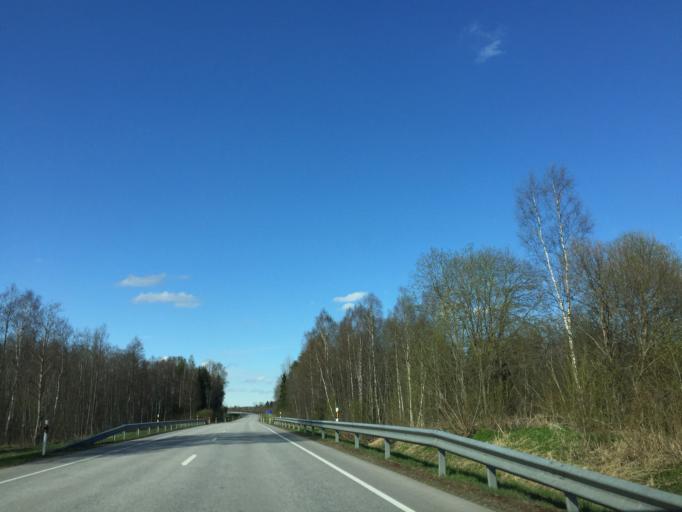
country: EE
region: Vorumaa
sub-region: Antsla vald
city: Vana-Antsla
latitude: 57.8879
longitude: 26.2861
